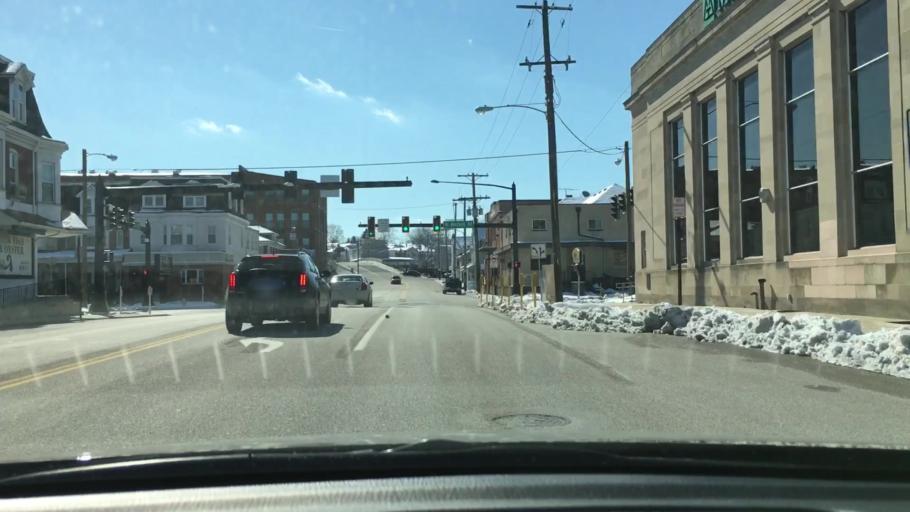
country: US
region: Pennsylvania
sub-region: York County
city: West York
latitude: 39.9541
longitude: -76.7593
